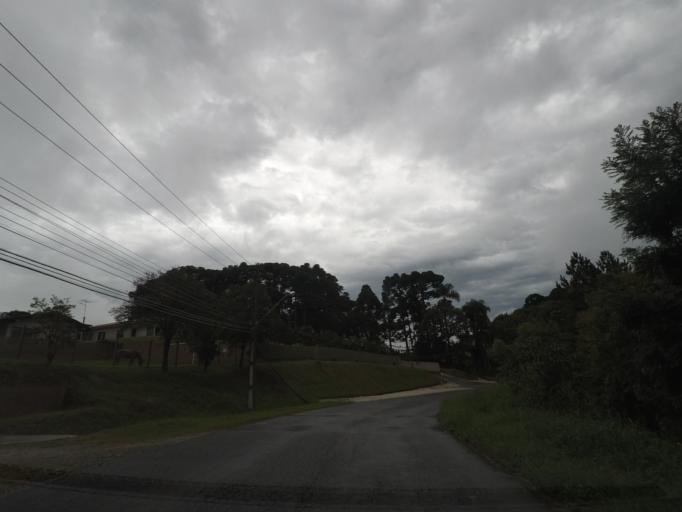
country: BR
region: Parana
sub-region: Campo Largo
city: Campo Largo
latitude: -25.4526
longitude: -49.4534
